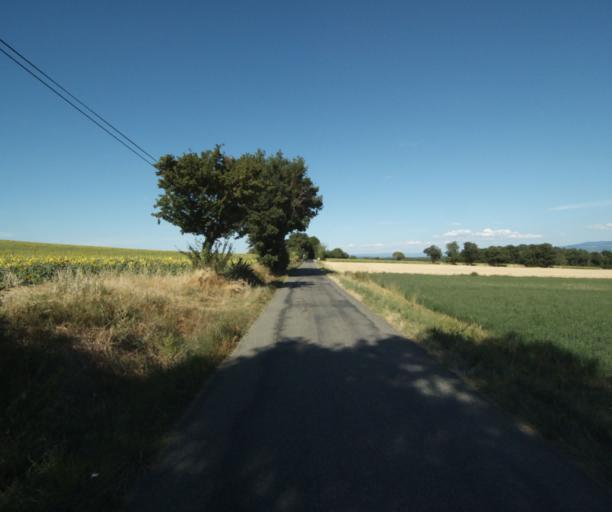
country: FR
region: Midi-Pyrenees
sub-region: Departement de la Haute-Garonne
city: Saint-Felix-Lauragais
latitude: 43.4946
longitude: 1.9414
